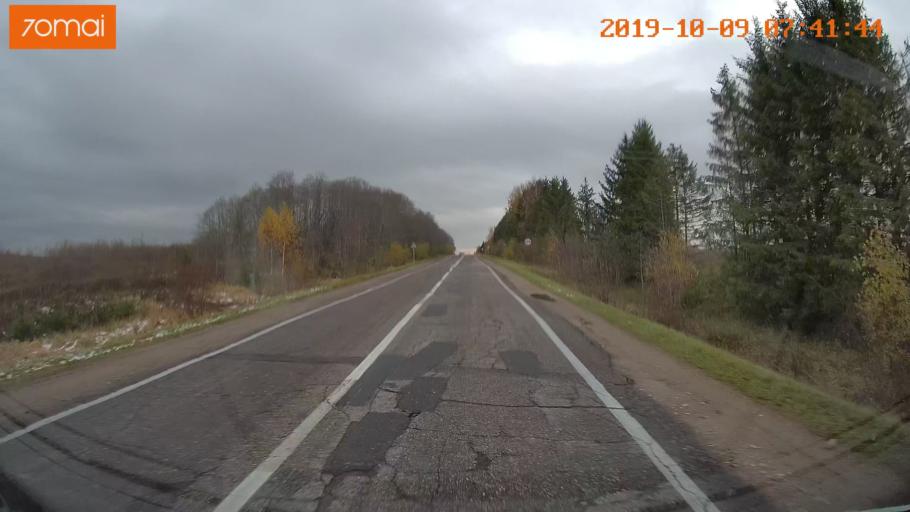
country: RU
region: Jaroslavl
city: Kukoboy
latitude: 58.6400
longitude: 39.7113
